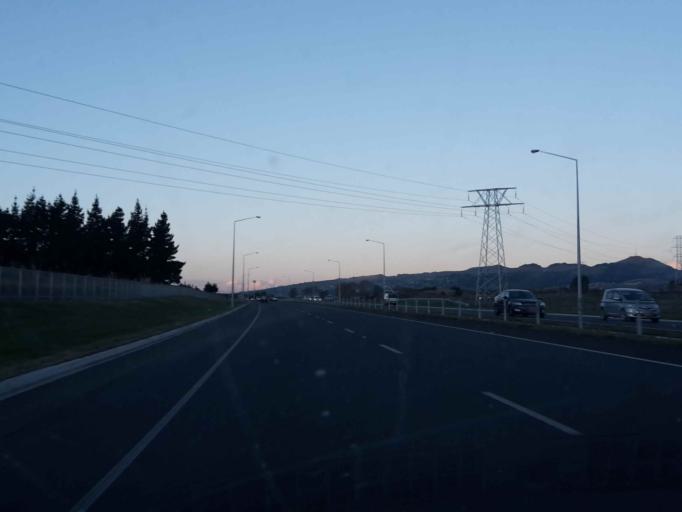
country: NZ
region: Canterbury
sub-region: Selwyn District
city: Prebbleton
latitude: -43.5646
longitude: 172.5431
